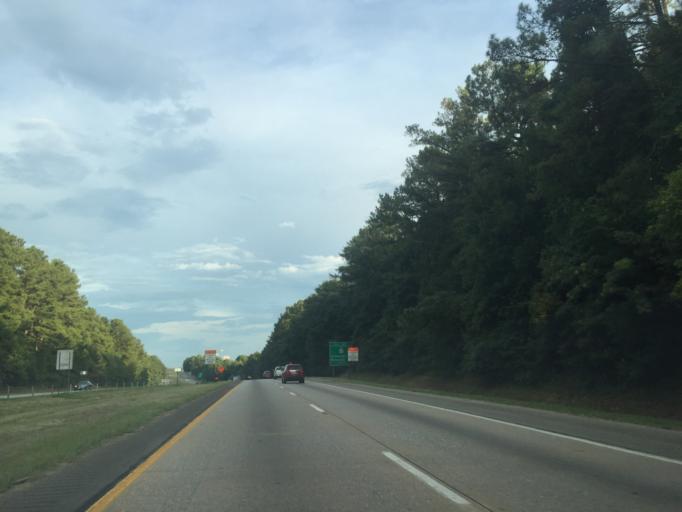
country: US
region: Georgia
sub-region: Bibb County
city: Macon
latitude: 32.9131
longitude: -83.7010
